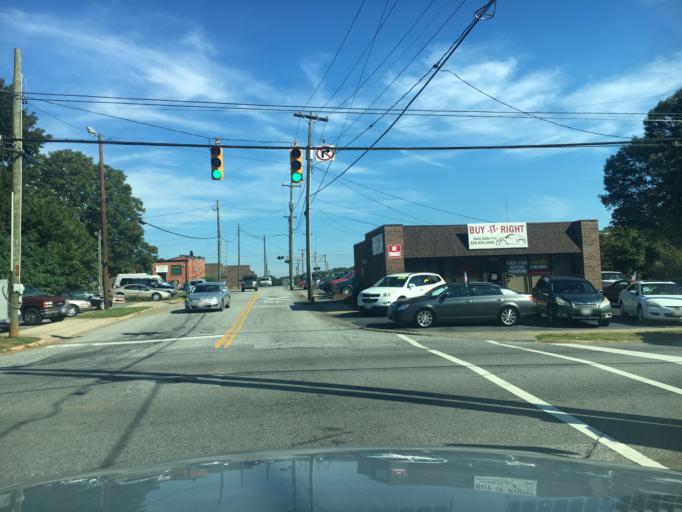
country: US
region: North Carolina
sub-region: Catawba County
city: Hickory
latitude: 35.7307
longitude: -81.3525
